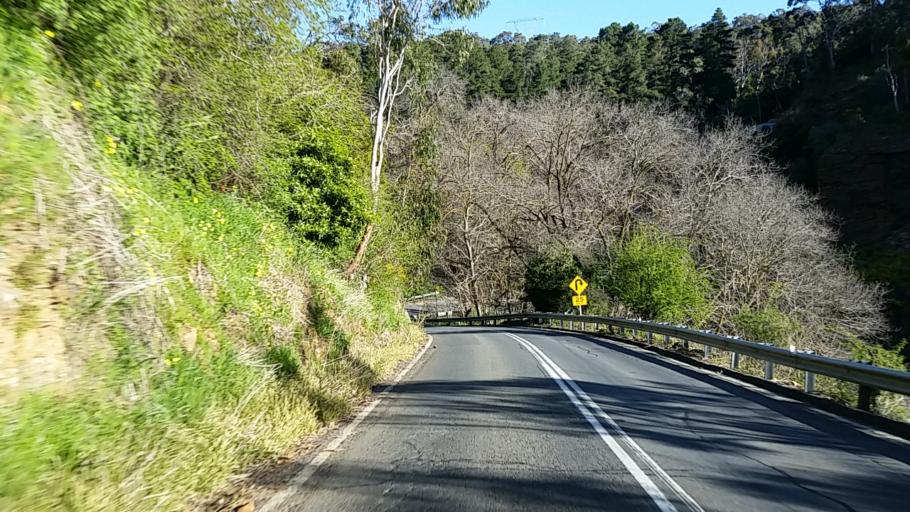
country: AU
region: South Australia
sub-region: Adelaide Hills
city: Adelaide Hills
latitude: -34.9260
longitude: 138.7190
